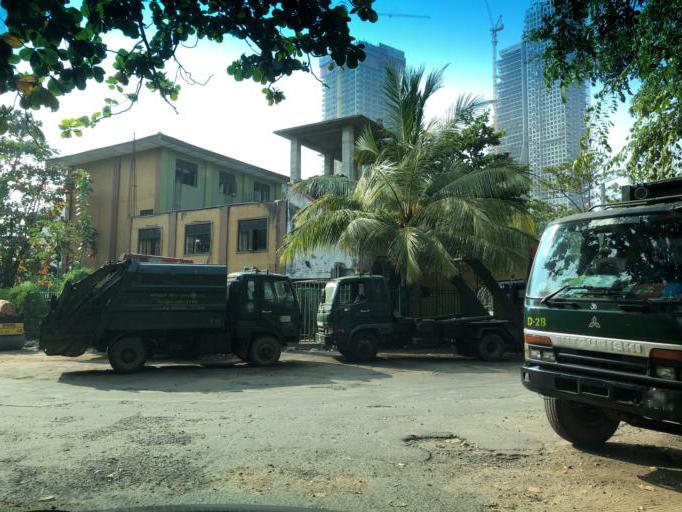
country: LK
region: Western
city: Colombo
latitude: 6.9165
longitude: 79.8582
